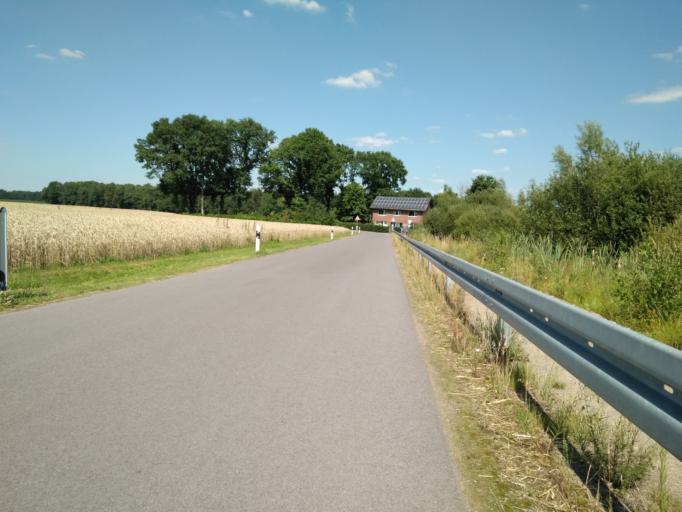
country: DE
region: North Rhine-Westphalia
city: Dorsten
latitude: 51.6840
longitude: 6.9783
